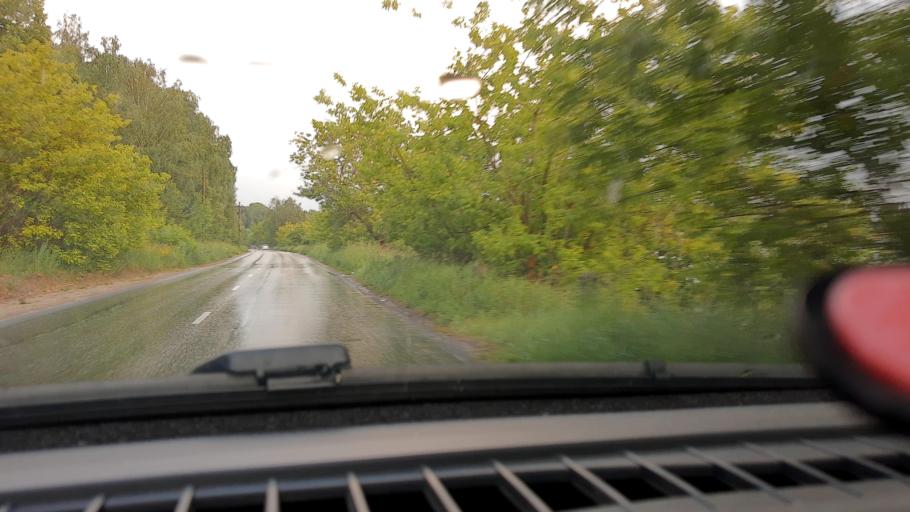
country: RU
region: Nizjnij Novgorod
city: Gorodets
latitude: 56.6709
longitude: 43.4496
